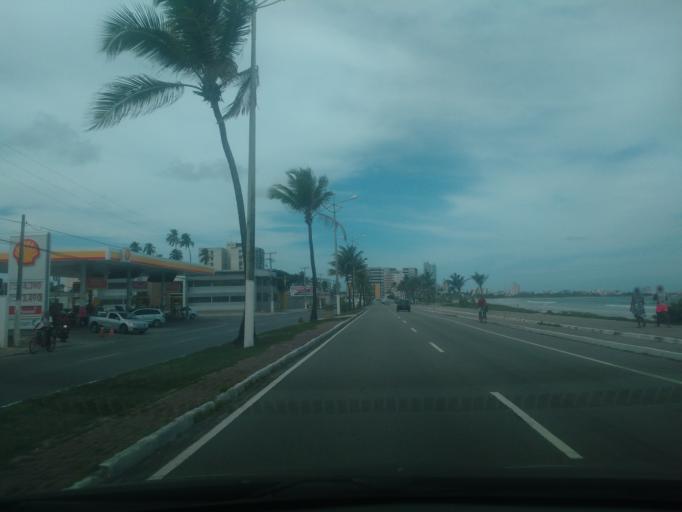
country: BR
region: Alagoas
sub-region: Maceio
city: Maceio
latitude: -9.6719
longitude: -35.7452
